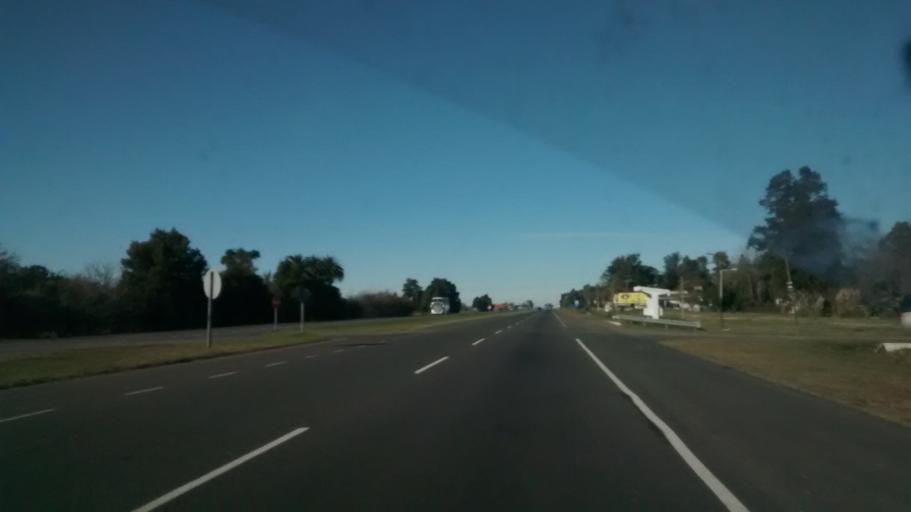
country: AR
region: Buenos Aires
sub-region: Partido de Chascomus
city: Chascomus
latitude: -35.7715
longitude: -57.9295
